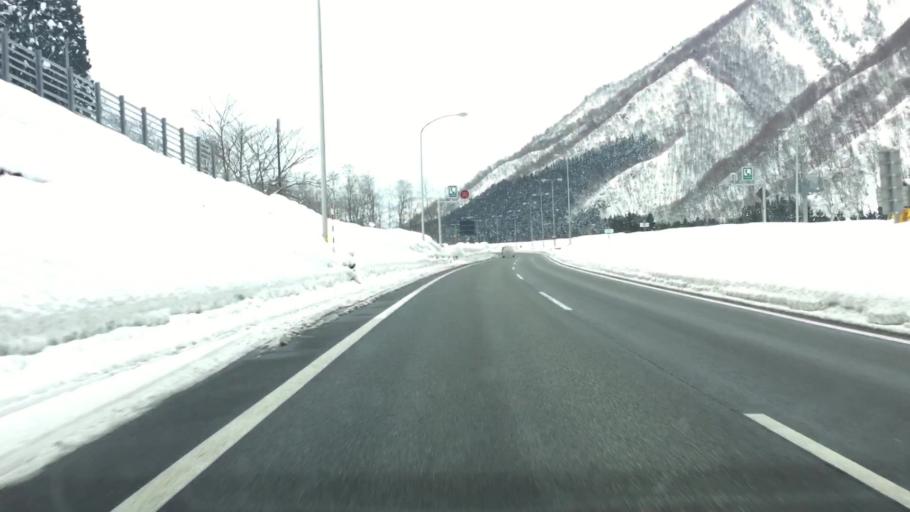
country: JP
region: Niigata
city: Shiozawa
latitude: 36.8712
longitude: 138.8650
